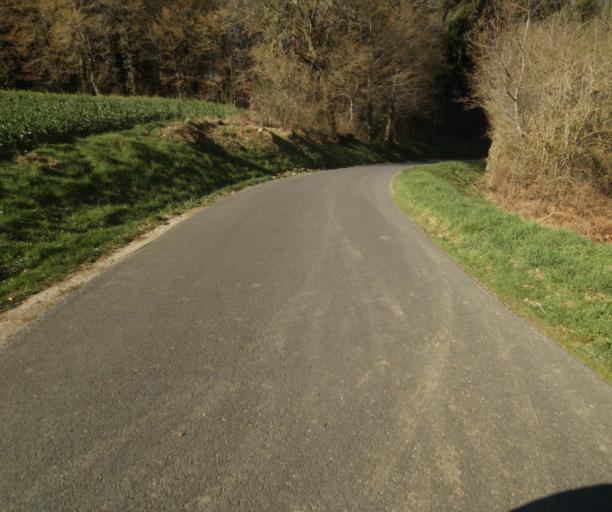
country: FR
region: Limousin
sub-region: Departement de la Correze
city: Tulle
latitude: 45.2846
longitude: 1.7209
